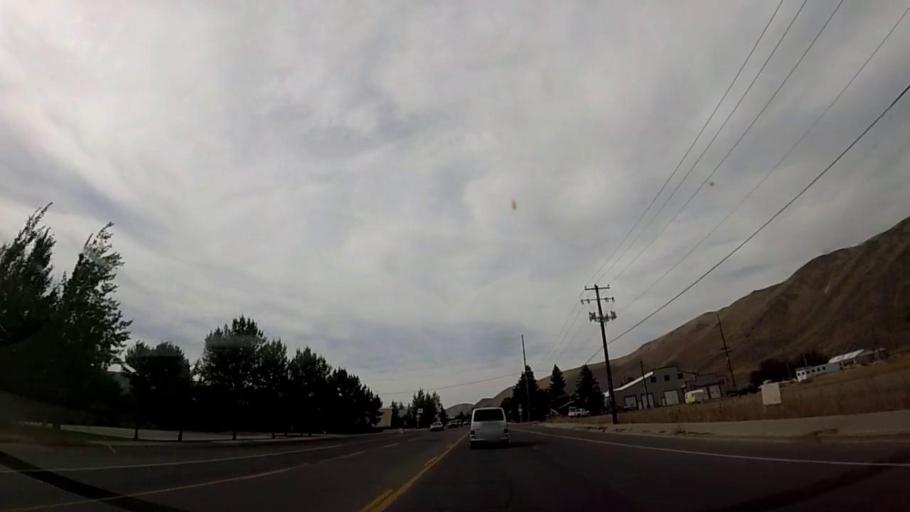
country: US
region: Idaho
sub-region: Blaine County
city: Bellevue
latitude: 43.4699
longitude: -114.2633
